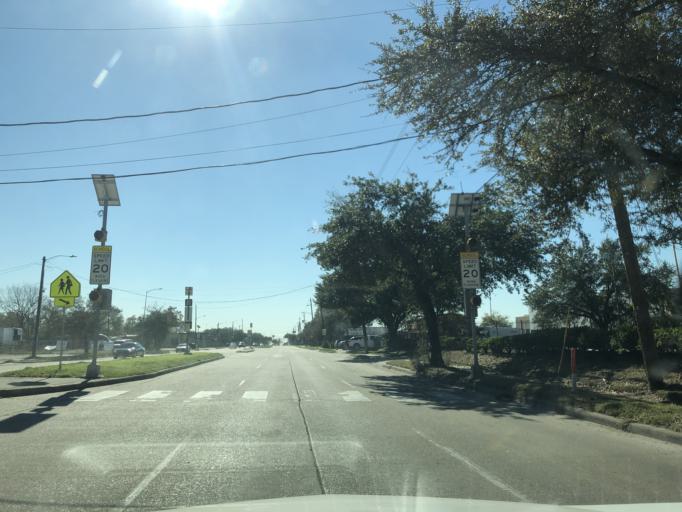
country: US
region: Texas
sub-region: Harris County
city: Houston
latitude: 29.8202
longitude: -95.3021
